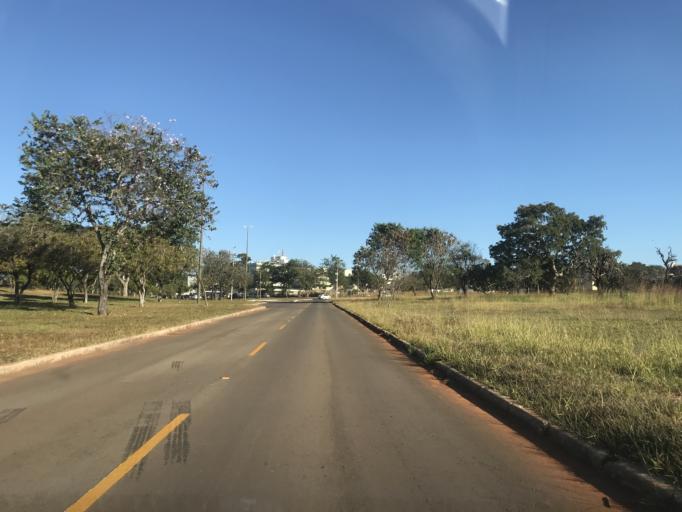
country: BR
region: Federal District
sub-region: Brasilia
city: Brasilia
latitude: -15.8305
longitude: -47.9006
